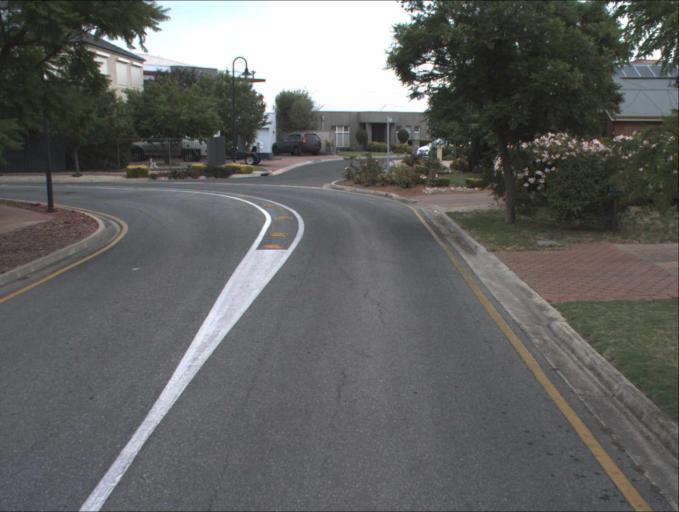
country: AU
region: South Australia
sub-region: Port Adelaide Enfield
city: Gilles Plains
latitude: -34.8559
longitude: 138.6278
